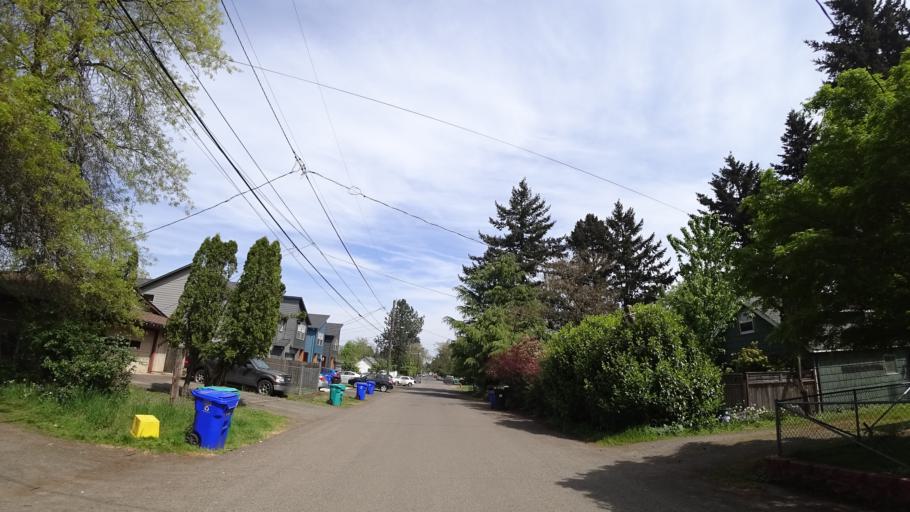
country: US
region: Oregon
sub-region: Multnomah County
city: Lents
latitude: 45.4700
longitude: -122.6058
